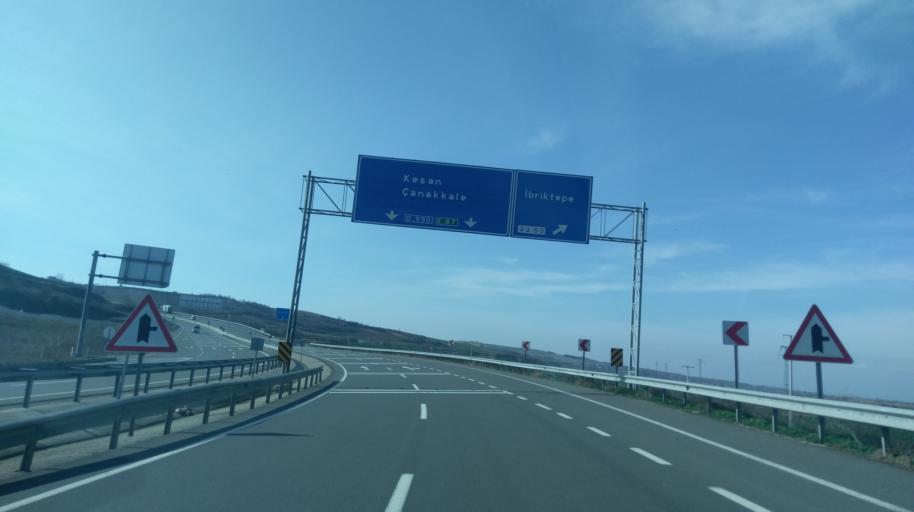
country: TR
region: Edirne
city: Hamidiye
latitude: 41.1090
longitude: 26.6407
